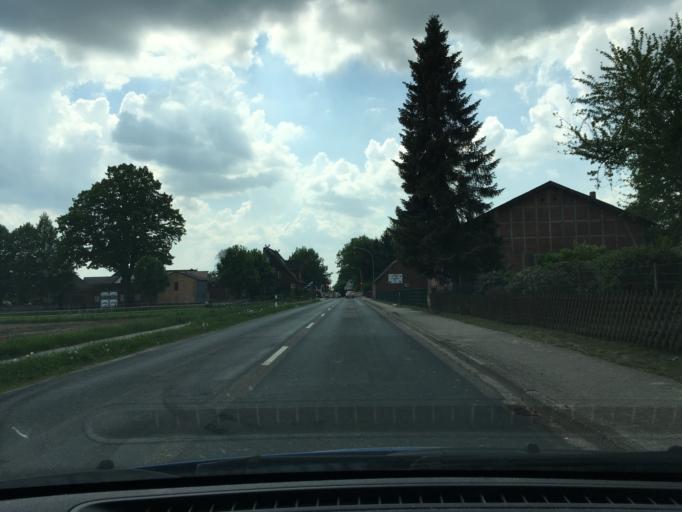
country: DE
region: Lower Saxony
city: Seevetal
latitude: 53.4234
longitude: 9.8979
